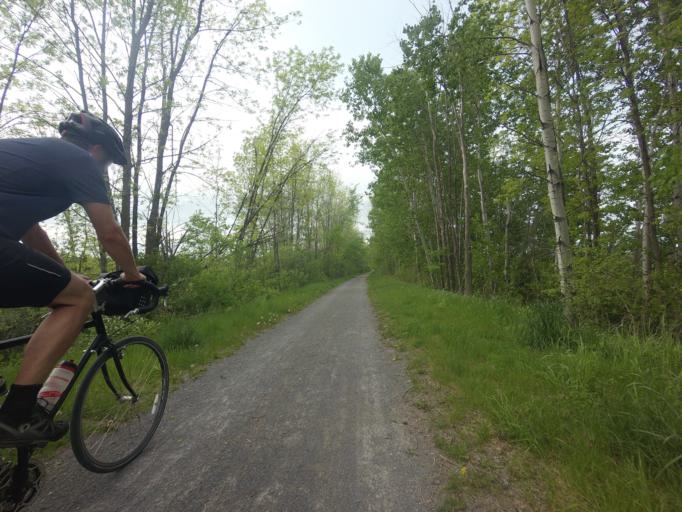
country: CA
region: Ontario
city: Kingston
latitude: 44.3183
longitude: -76.5864
